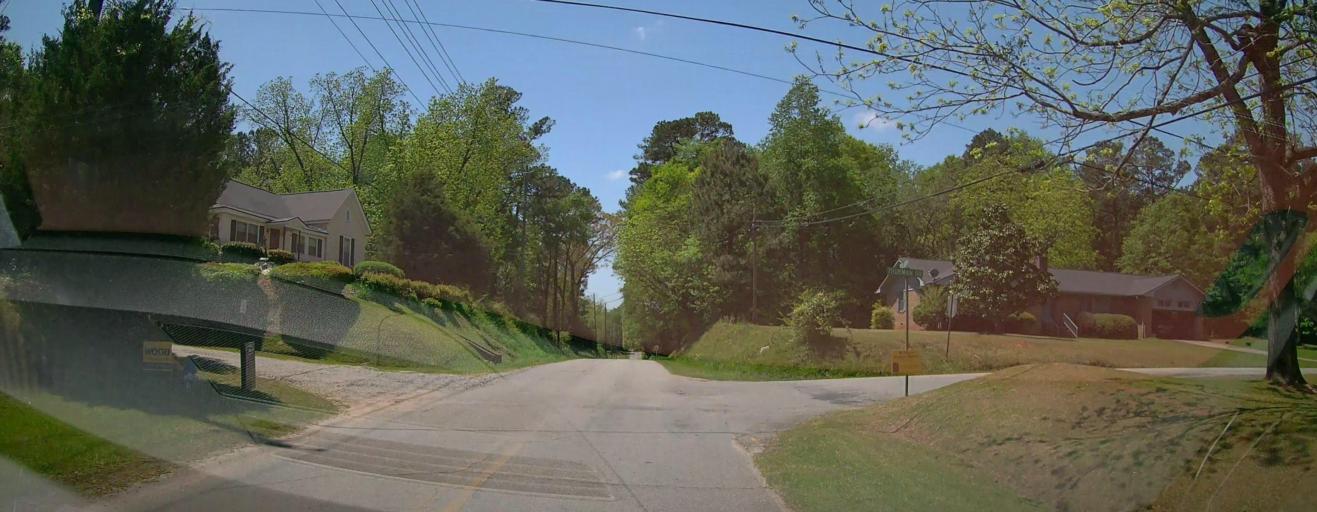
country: US
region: Georgia
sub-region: Jones County
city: Gray
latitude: 33.0031
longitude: -83.5526
